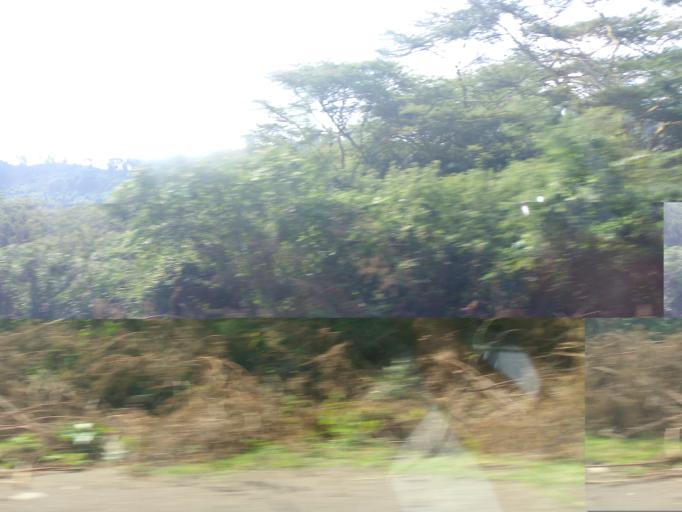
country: KE
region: Kiambu
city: Limuru
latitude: -1.0298
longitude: 36.6024
